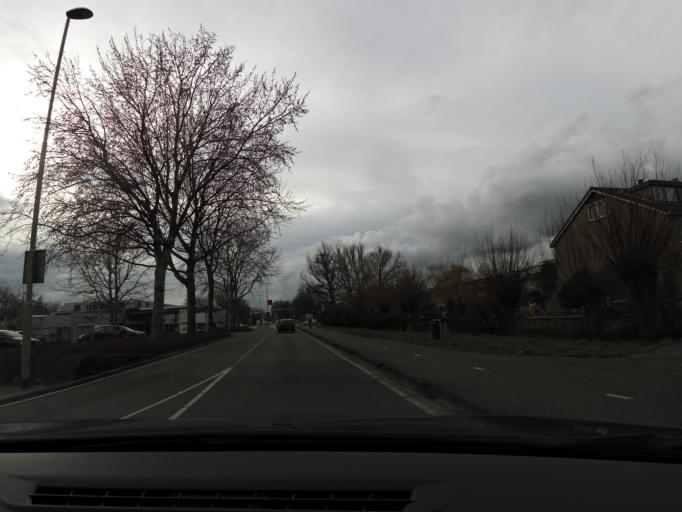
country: NL
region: South Holland
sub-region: Gemeente Gouda
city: Gouda
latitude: 52.0285
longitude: 4.7158
